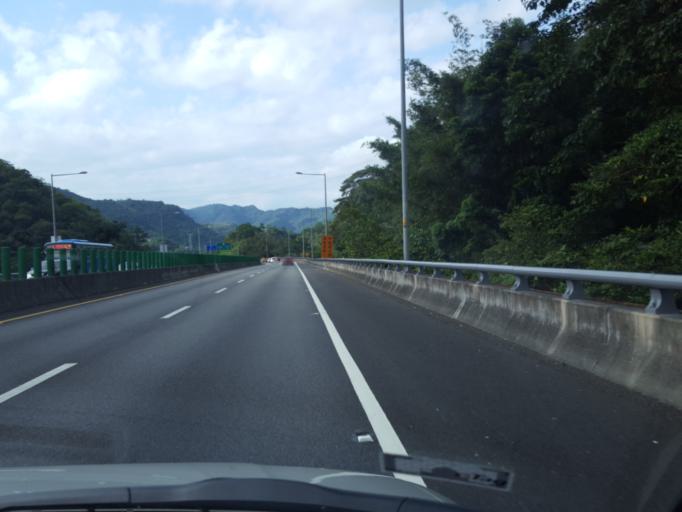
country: TW
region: Taipei
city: Taipei
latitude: 24.9869
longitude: 121.6596
